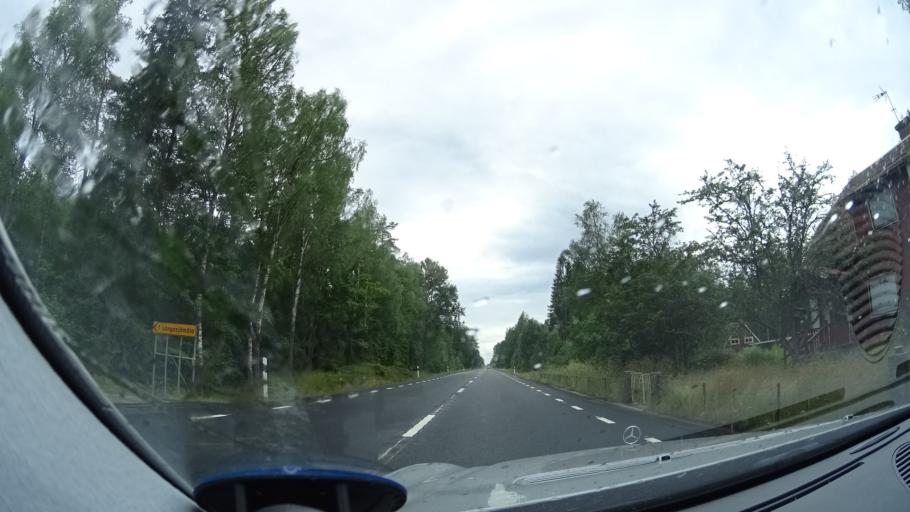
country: SE
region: Kronoberg
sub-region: Tingsryds Kommun
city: Tingsryd
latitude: 56.4077
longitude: 14.9358
